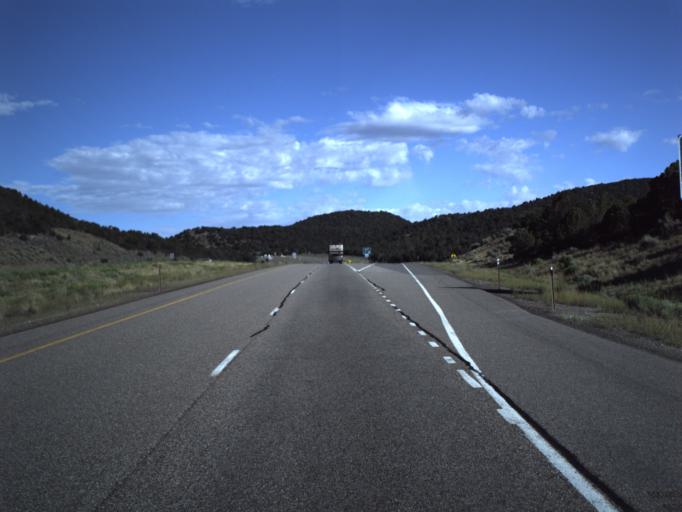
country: US
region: Utah
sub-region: Beaver County
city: Beaver
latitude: 38.5842
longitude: -112.4860
